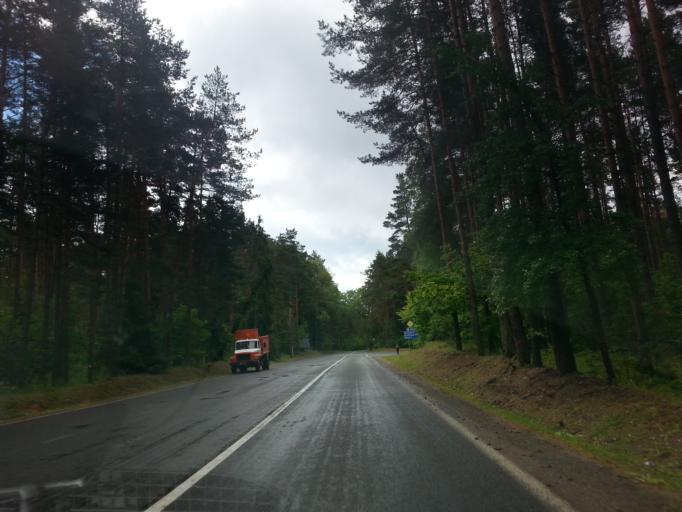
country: BY
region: Minsk
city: Narach
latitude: 54.9161
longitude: 26.7189
